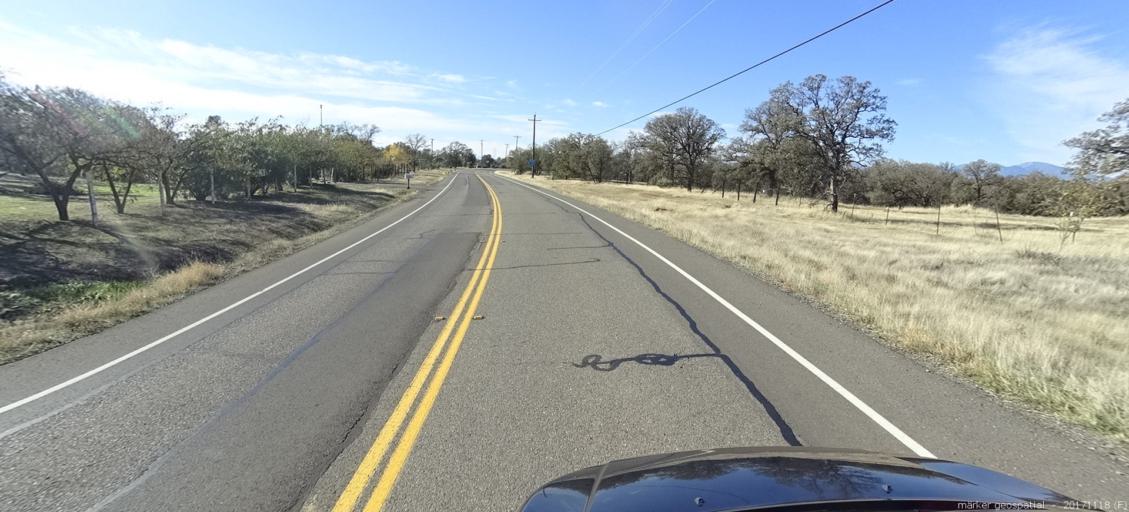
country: US
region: California
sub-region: Shasta County
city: Anderson
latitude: 40.4409
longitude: -122.3377
